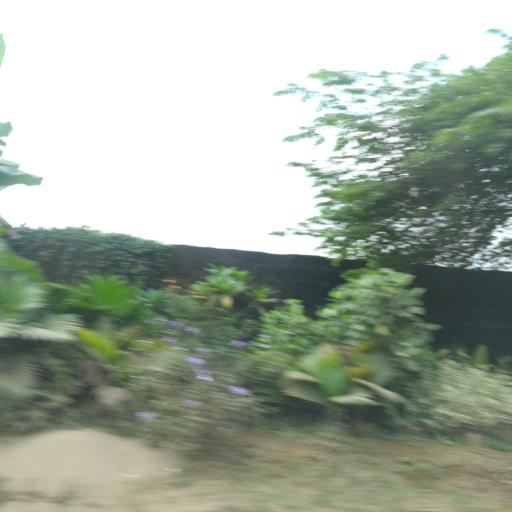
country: NG
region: Rivers
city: Okrika
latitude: 4.7838
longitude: 7.1343
